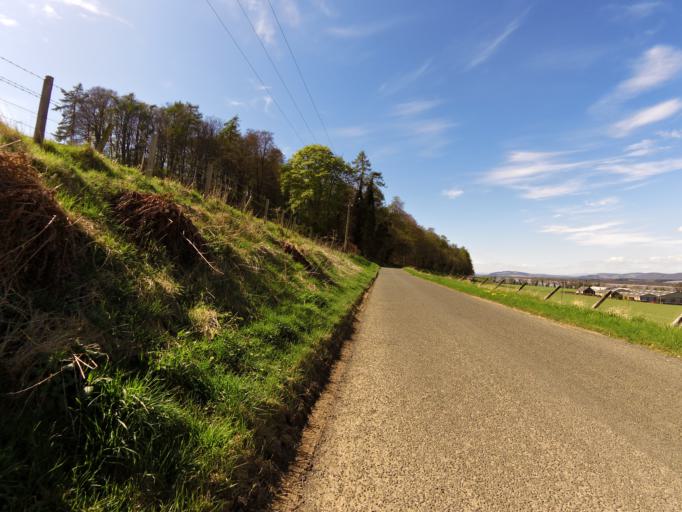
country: GB
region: Scotland
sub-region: Perth and Kinross
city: Errol
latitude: 56.3678
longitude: -3.1734
